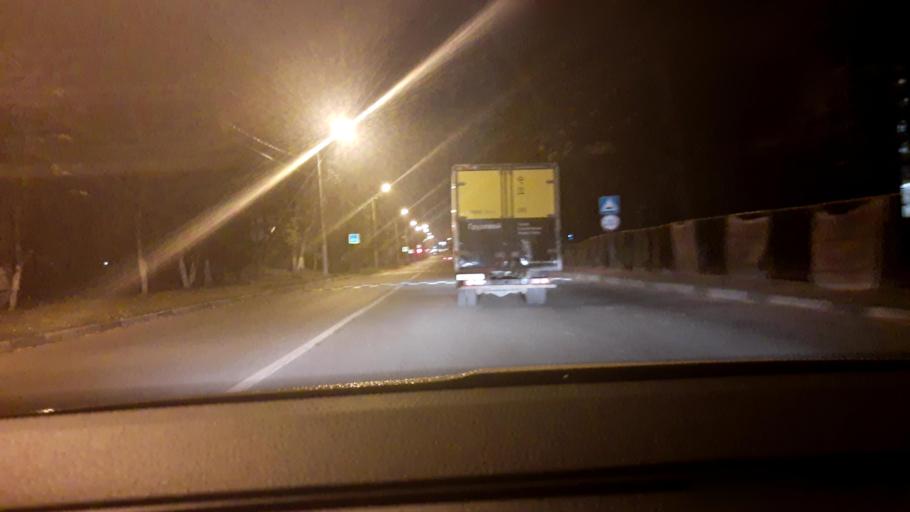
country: RU
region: Moskovskaya
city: Dolgoprudnyy
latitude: 55.9428
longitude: 37.5084
